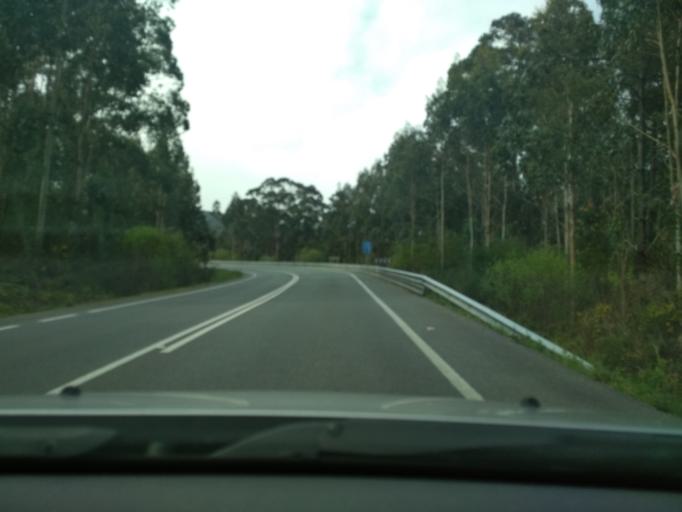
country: ES
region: Galicia
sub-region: Provincia de Pontevedra
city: Catoira
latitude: 42.6555
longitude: -8.7047
